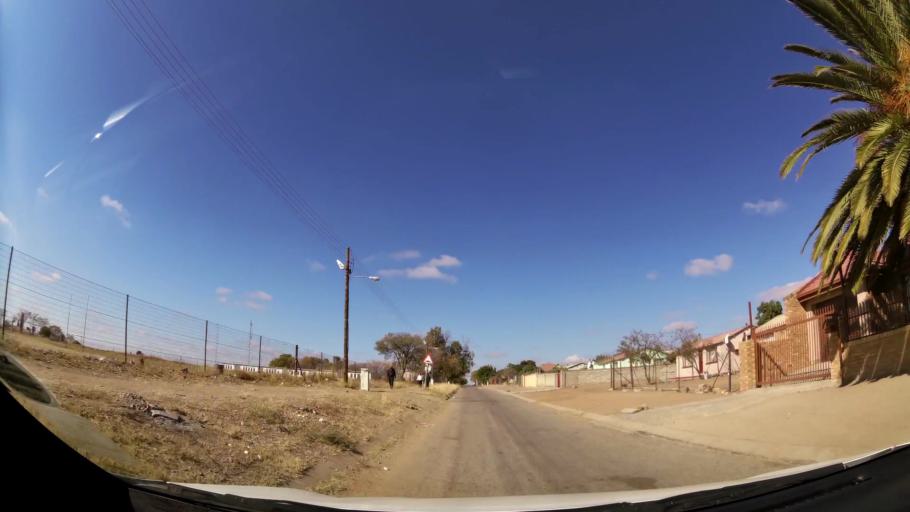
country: ZA
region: Limpopo
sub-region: Capricorn District Municipality
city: Polokwane
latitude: -23.8617
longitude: 29.3879
